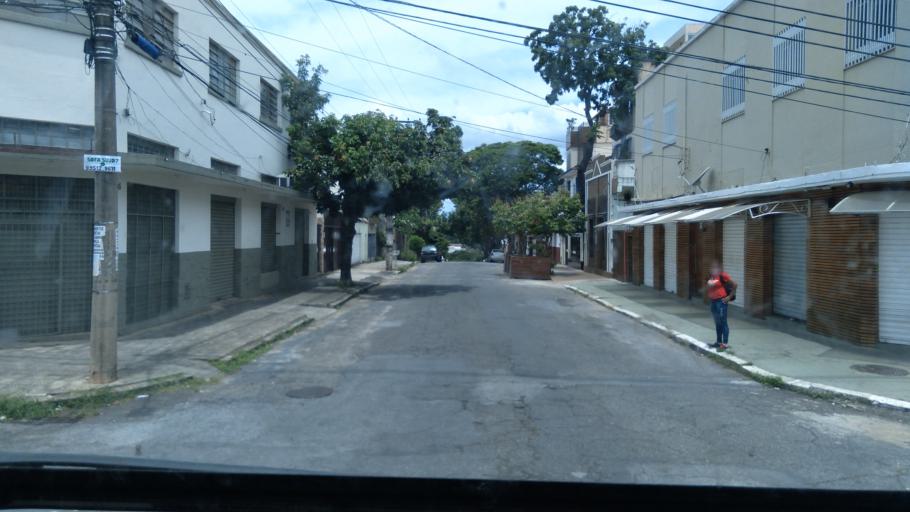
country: BR
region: Minas Gerais
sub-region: Belo Horizonte
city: Belo Horizonte
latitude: -19.9171
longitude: -43.9135
